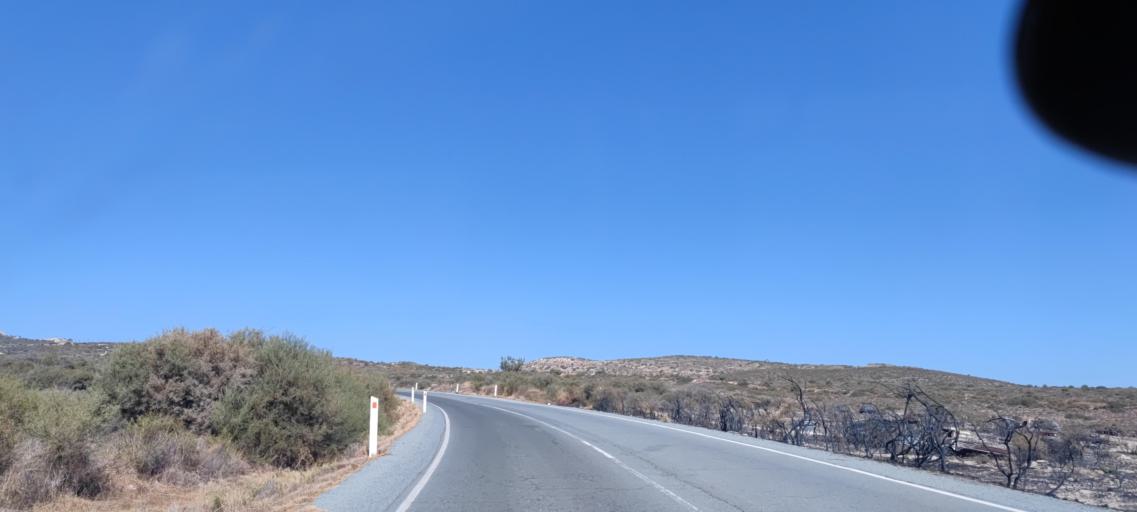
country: CY
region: Limassol
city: Mouttagiaka
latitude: 34.7360
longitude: 33.0646
